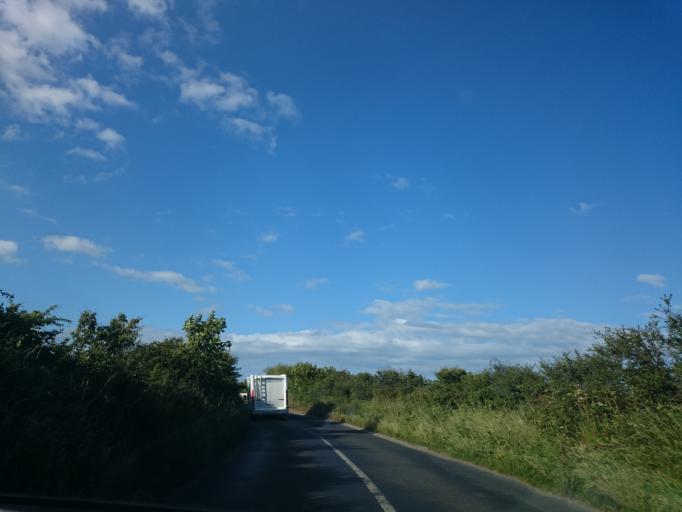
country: IE
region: Leinster
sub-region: Loch Garman
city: Loch Garman
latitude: 52.1953
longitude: -6.5582
